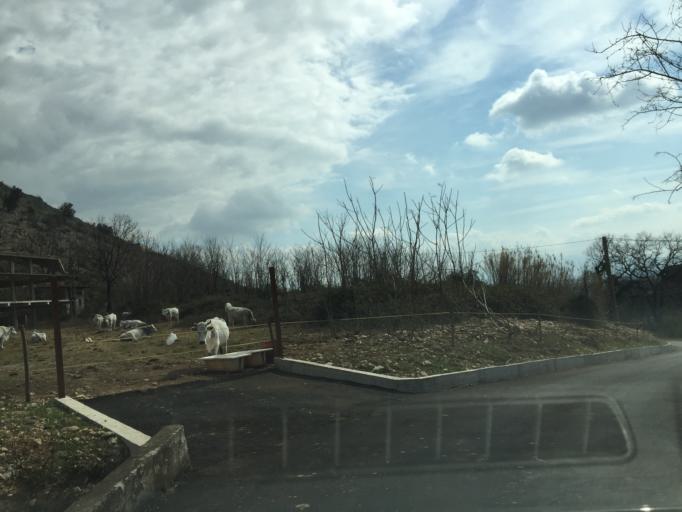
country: IT
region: Latium
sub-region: Provincia di Frosinone
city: Castrocielo
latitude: 41.5242
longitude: 13.7034
